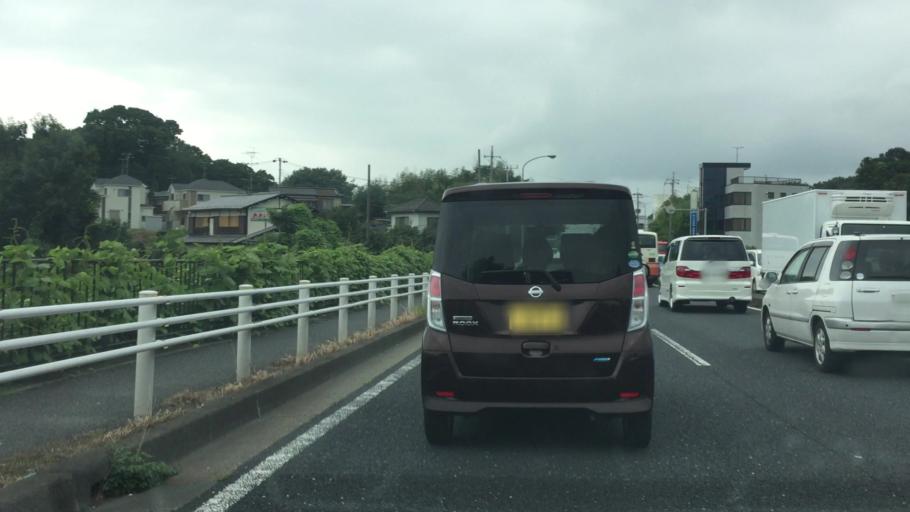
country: JP
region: Chiba
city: Abiko
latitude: 35.8343
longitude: 140.0092
